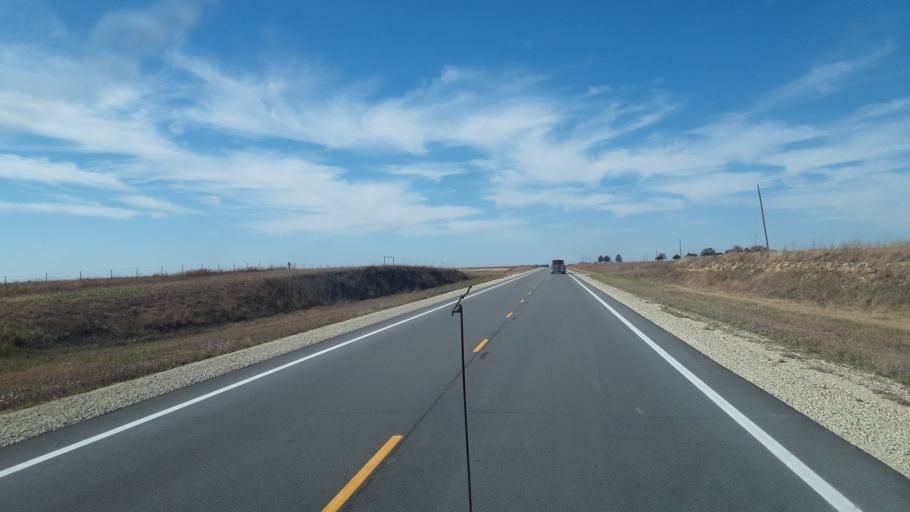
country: US
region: Kansas
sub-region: Marion County
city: Marion
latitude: 38.3630
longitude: -96.8244
